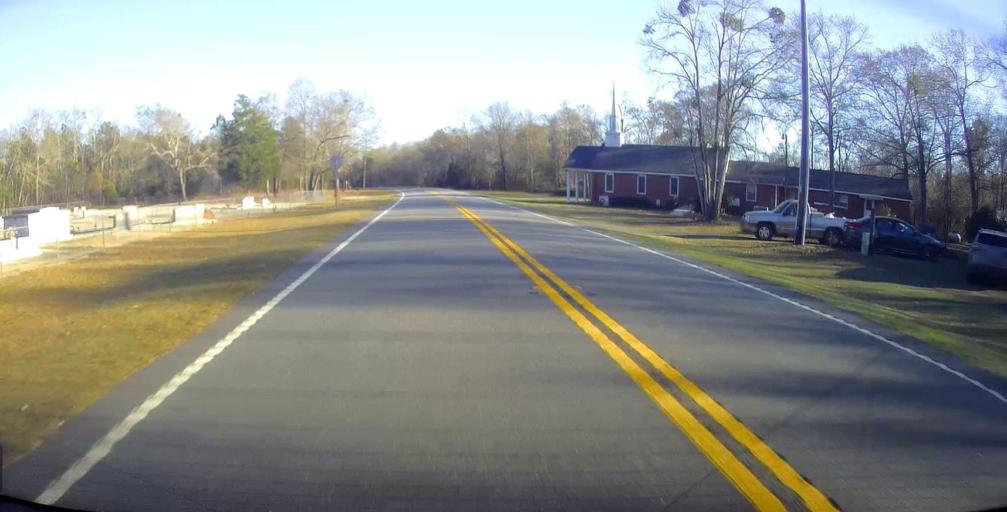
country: US
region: Georgia
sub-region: Taylor County
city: Butler
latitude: 32.4785
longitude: -84.3894
